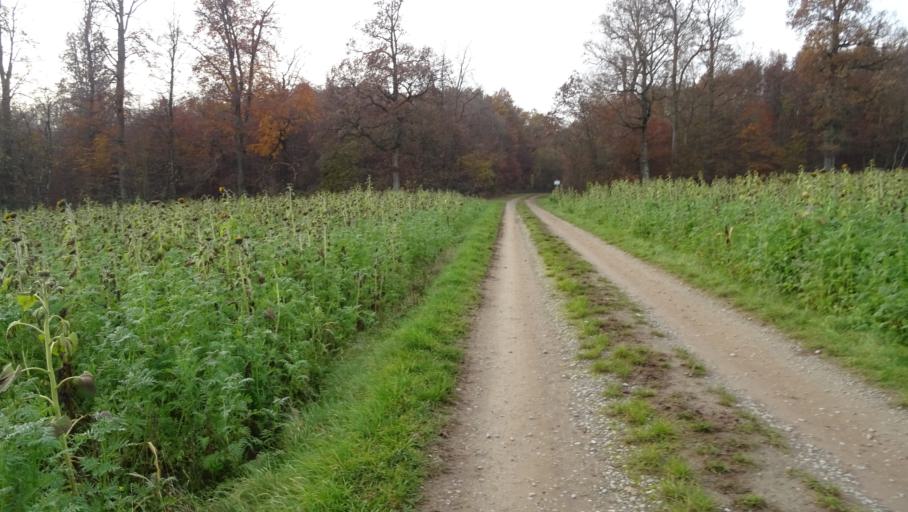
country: DE
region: Baden-Wuerttemberg
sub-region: Karlsruhe Region
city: Neckargerach
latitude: 49.4162
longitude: 9.0694
